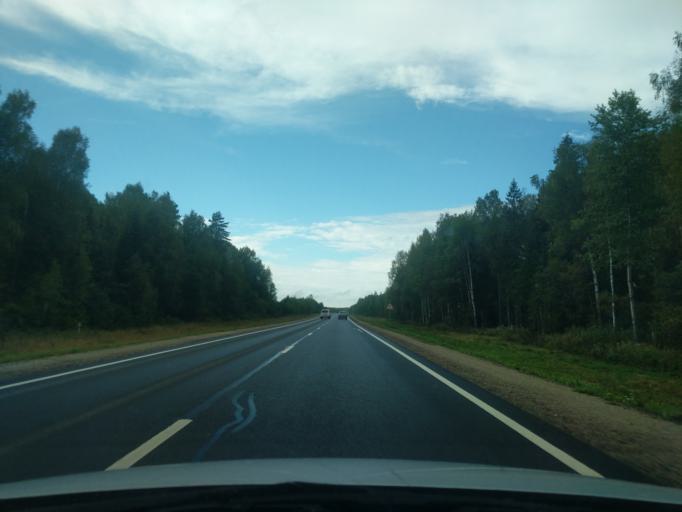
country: RU
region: Kostroma
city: Ostrovskoye
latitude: 57.8141
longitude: 42.0068
